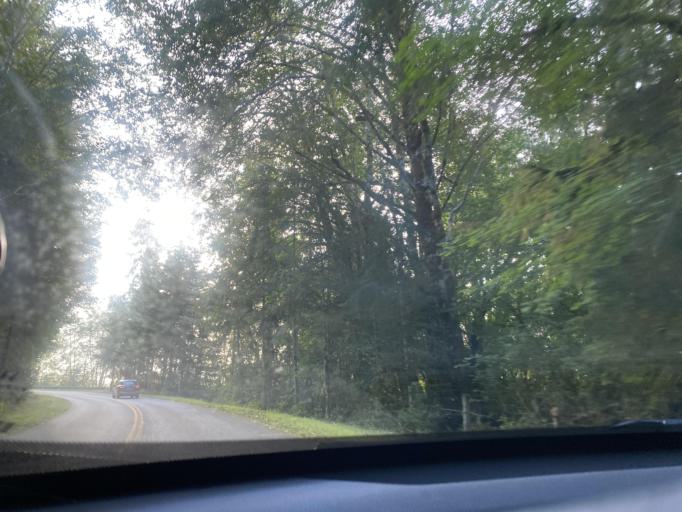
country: US
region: Washington
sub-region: Clallam County
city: Forks
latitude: 47.8172
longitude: -124.0369
